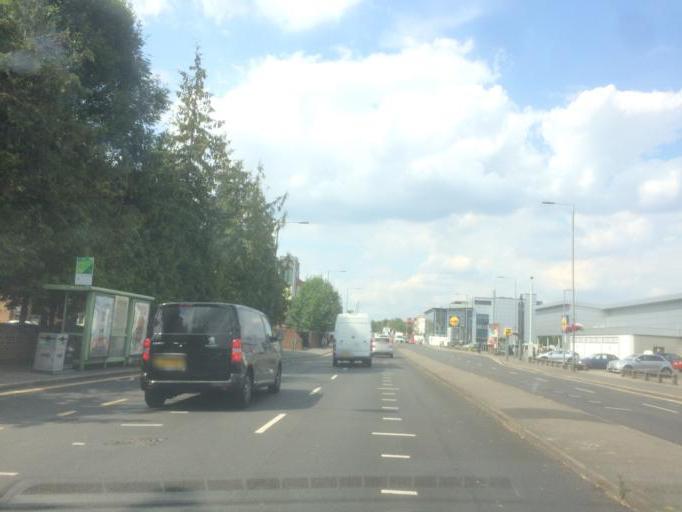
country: GB
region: England
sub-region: Buckinghamshire
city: Farnham Royal
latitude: 51.5262
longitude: -0.6160
